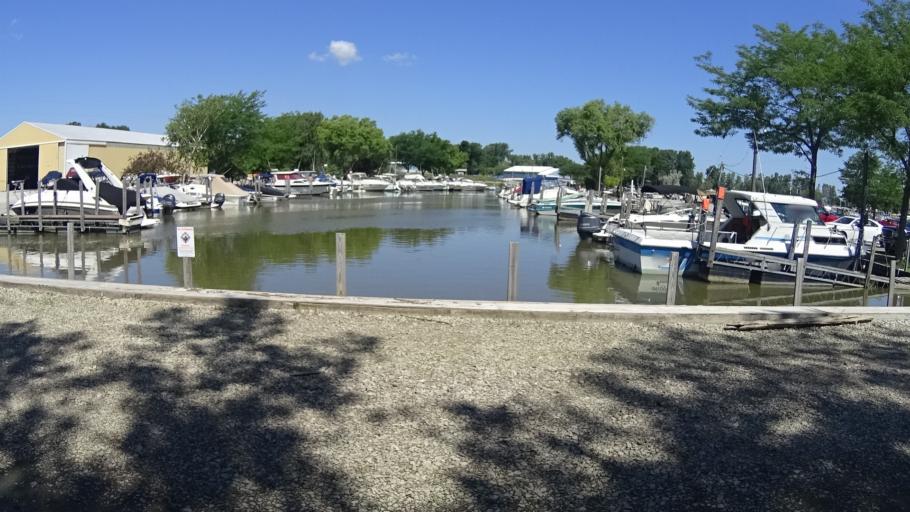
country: US
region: Ohio
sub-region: Erie County
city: Huron
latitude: 41.3850
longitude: -82.5542
